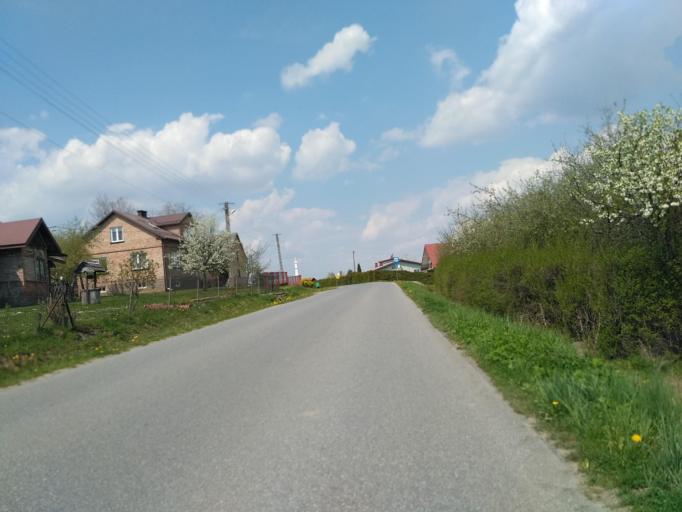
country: PL
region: Subcarpathian Voivodeship
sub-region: Powiat jasielski
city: Debowiec
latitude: 49.6966
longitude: 21.5088
